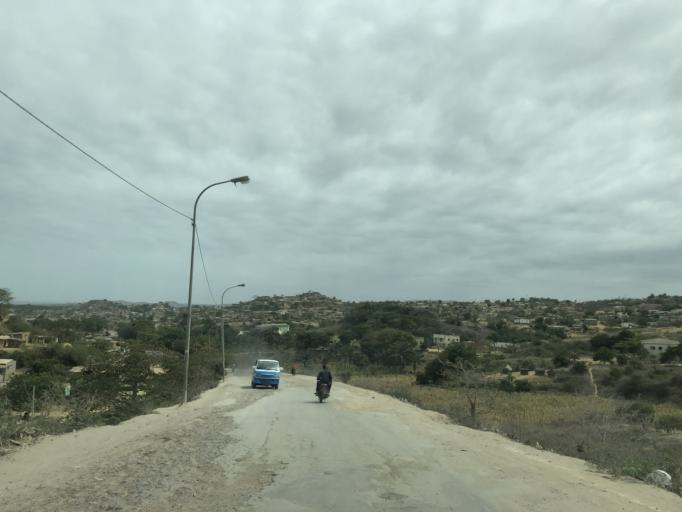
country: AO
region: Cuanza Sul
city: Sumbe
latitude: -11.2217
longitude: 13.8474
